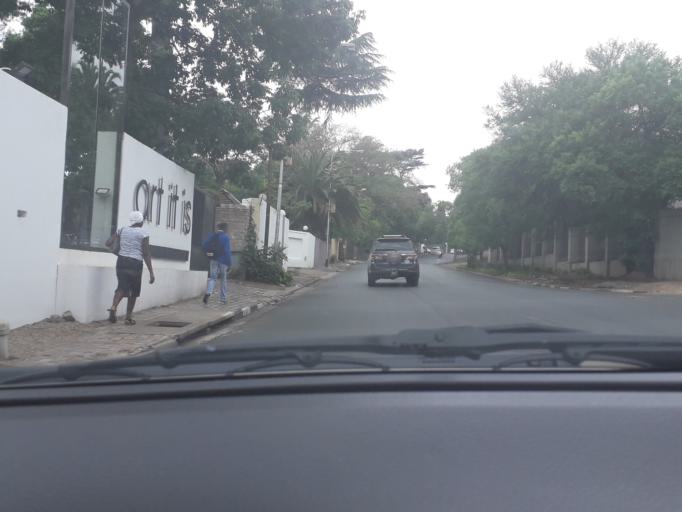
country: ZA
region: Gauteng
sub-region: City of Johannesburg Metropolitan Municipality
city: Johannesburg
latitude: -26.1495
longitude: 28.0269
